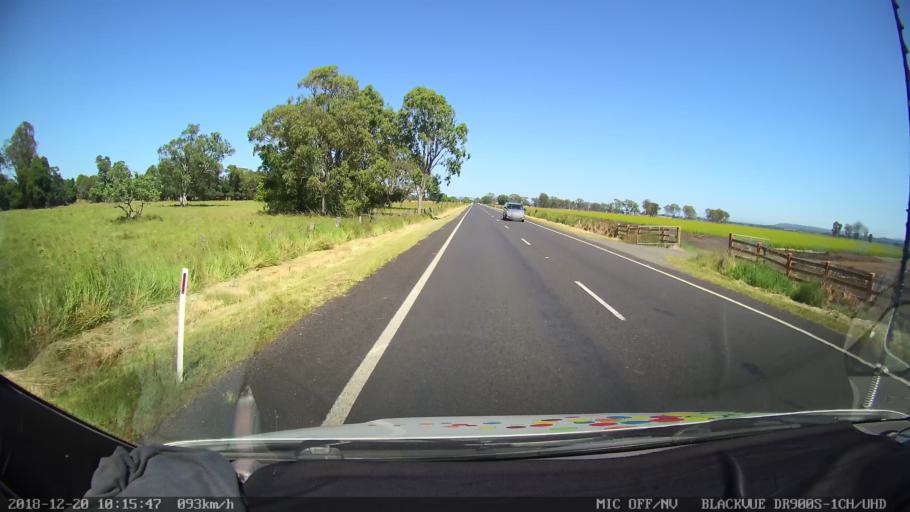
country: AU
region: New South Wales
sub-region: Richmond Valley
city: Casino
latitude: -28.8656
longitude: 153.0941
